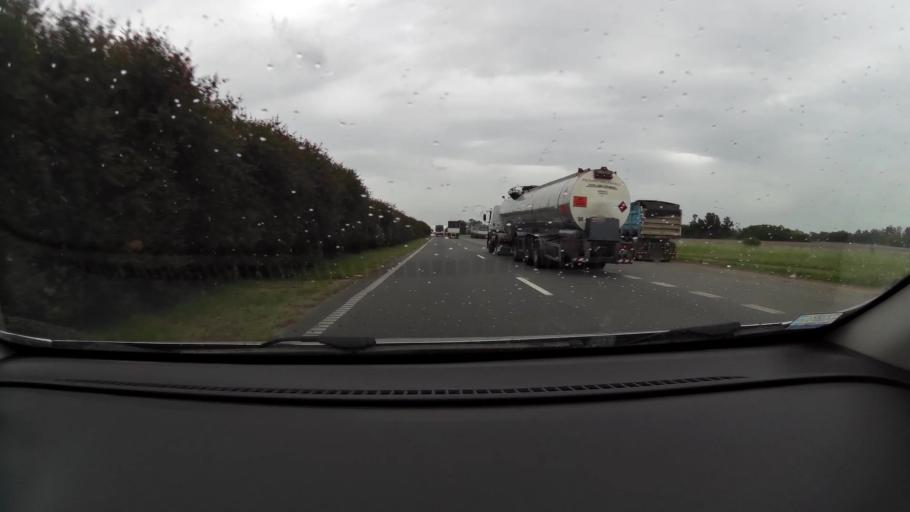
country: AR
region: Buenos Aires
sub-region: Partido de Baradero
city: Baradero
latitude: -33.8503
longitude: -59.5505
